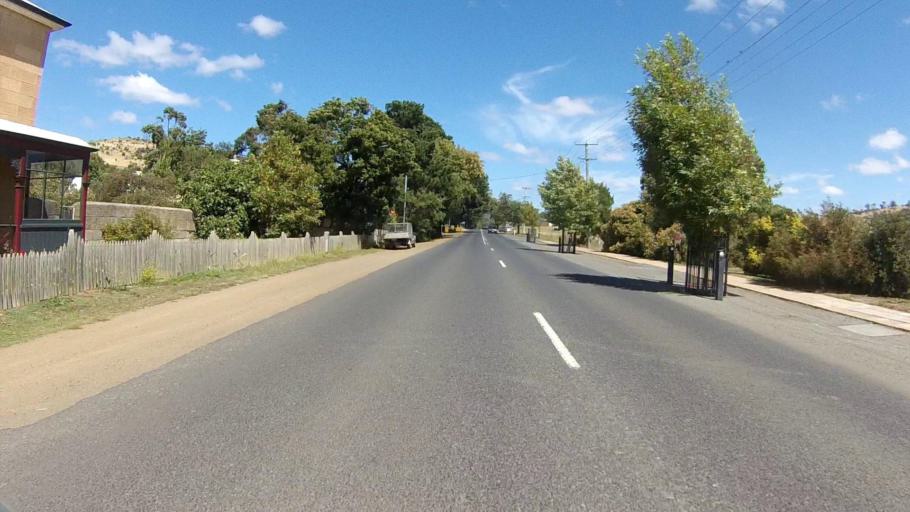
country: AU
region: Tasmania
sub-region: Clarence
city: Cambridge
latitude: -42.7374
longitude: 147.4331
